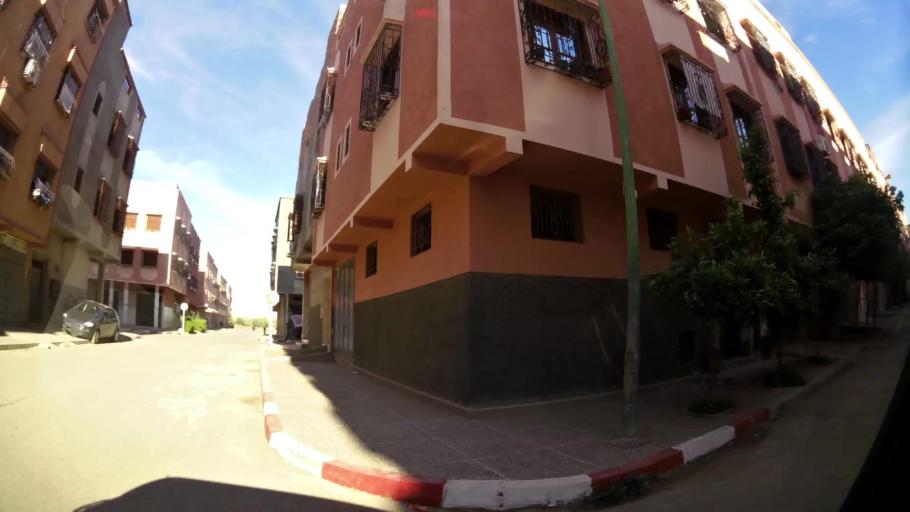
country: MA
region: Marrakech-Tensift-Al Haouz
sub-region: Marrakech
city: Marrakesh
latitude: 31.6241
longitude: -8.0696
